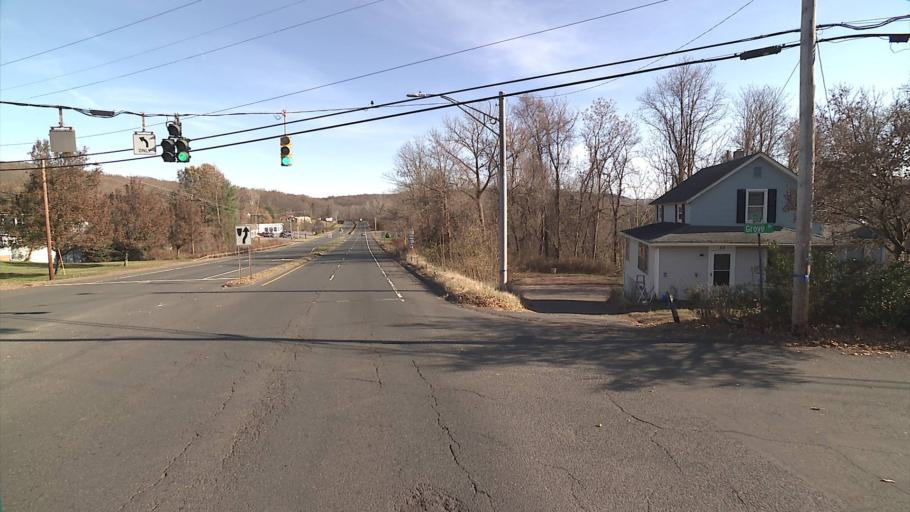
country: US
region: Connecticut
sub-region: Middlesex County
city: Portland
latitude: 41.5687
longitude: -72.6257
